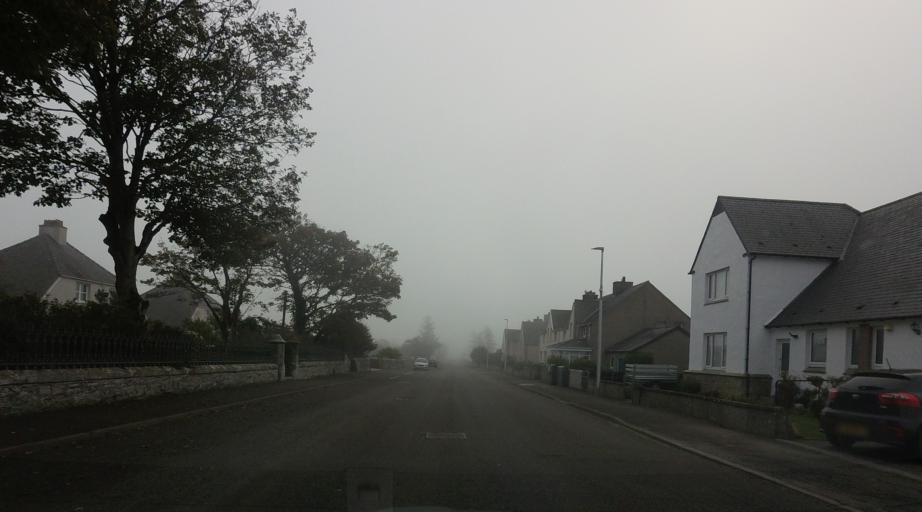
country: GB
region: Scotland
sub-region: Highland
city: Wick
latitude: 58.3070
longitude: -3.2855
